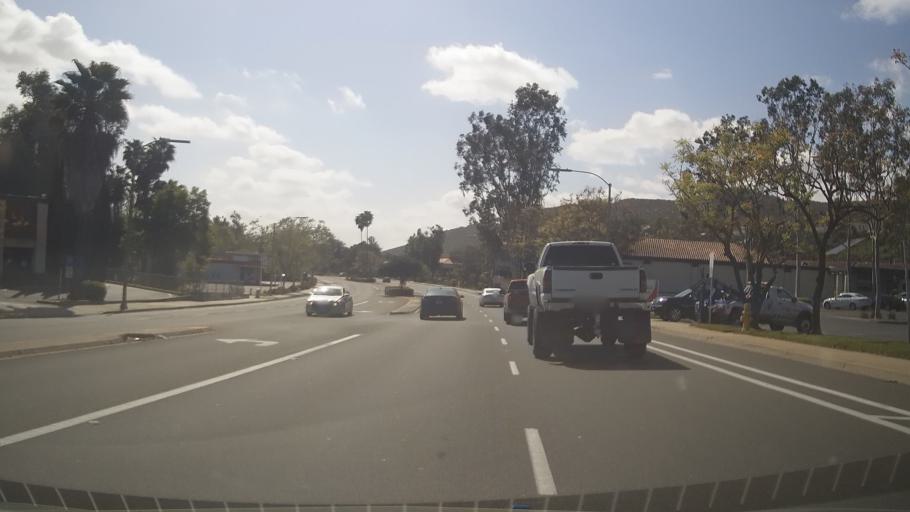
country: US
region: California
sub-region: San Diego County
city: Poway
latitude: 32.9519
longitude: -117.0640
